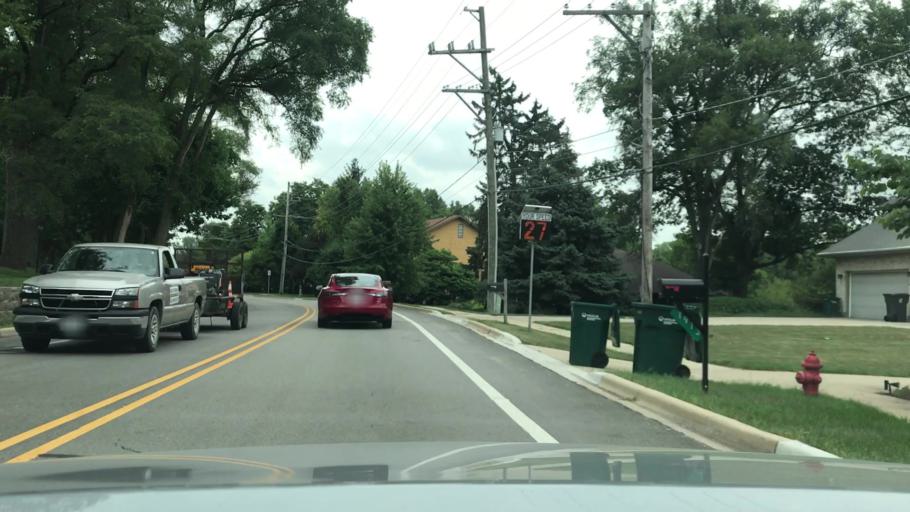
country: US
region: Illinois
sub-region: DuPage County
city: Darien
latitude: 41.7449
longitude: -87.9915
